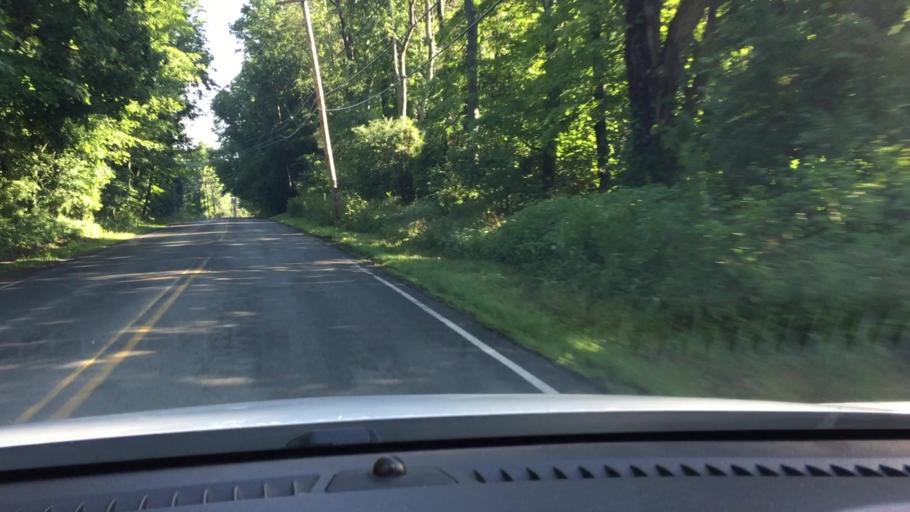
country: US
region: Massachusetts
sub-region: Berkshire County
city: Pittsfield
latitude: 42.4268
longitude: -73.2257
